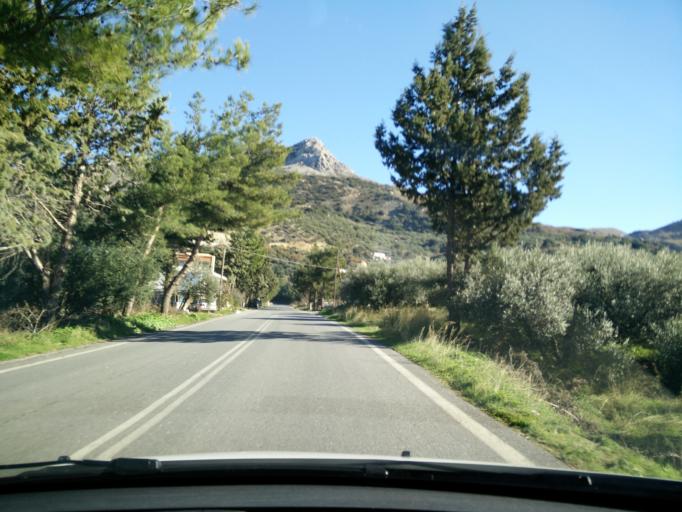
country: GR
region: Crete
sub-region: Nomos Irakleiou
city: Arkalochori
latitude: 35.0765
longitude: 25.3550
